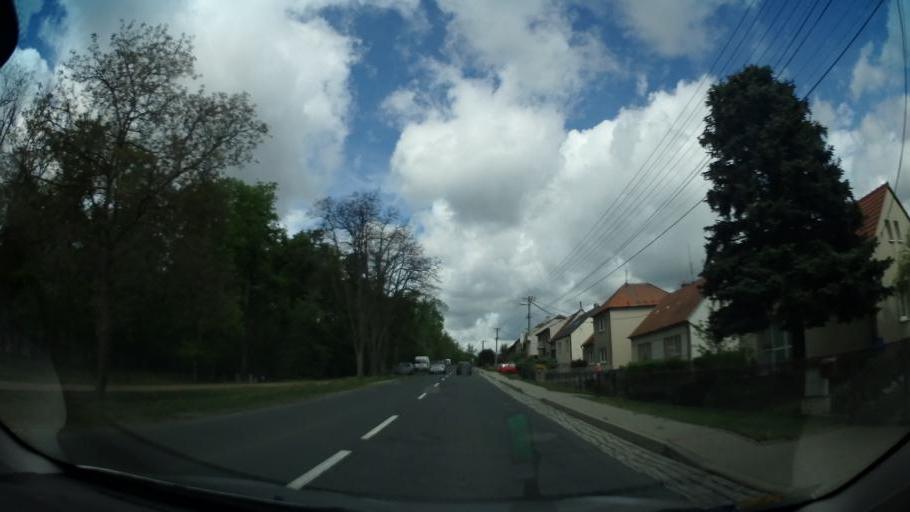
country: CZ
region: South Moravian
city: Ricany
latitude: 49.2335
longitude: 16.3555
